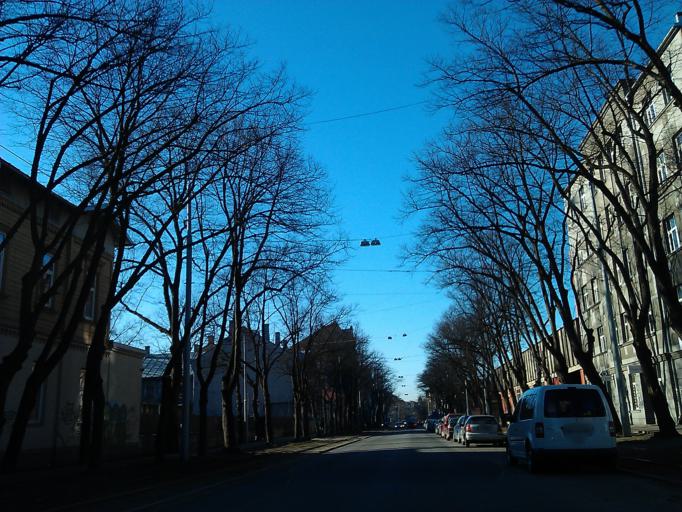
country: LV
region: Riga
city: Riga
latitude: 56.9681
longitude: 24.1351
